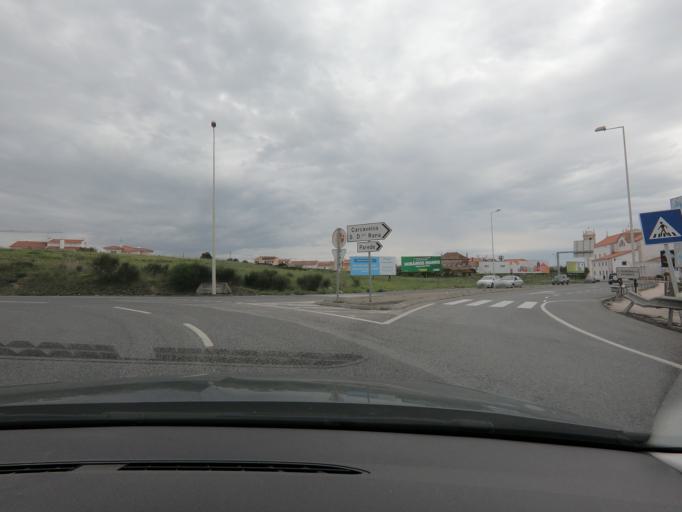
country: PT
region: Lisbon
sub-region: Cascais
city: Sao Domingos de Rana
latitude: 38.7042
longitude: -9.3406
